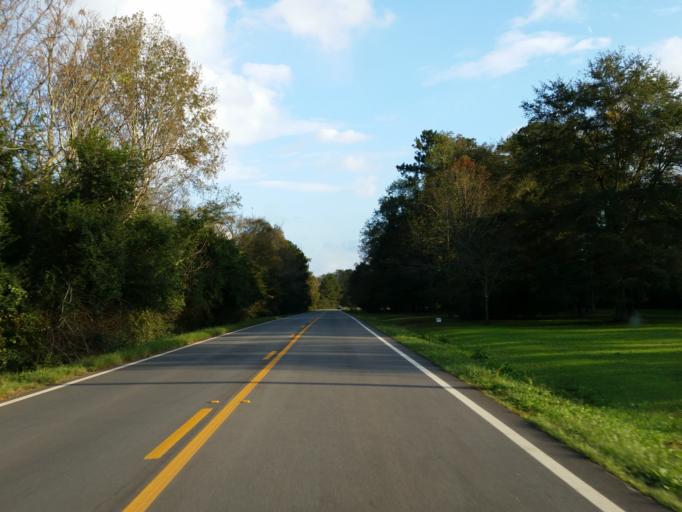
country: US
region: Georgia
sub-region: Monroe County
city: Forsyth
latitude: 32.9803
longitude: -83.8762
